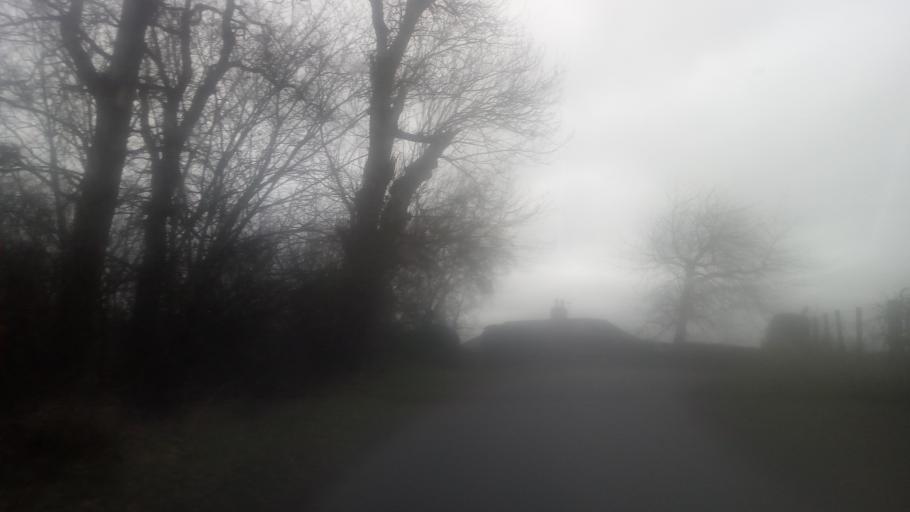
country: GB
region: Scotland
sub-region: The Scottish Borders
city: Jedburgh
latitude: 55.4848
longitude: -2.4832
